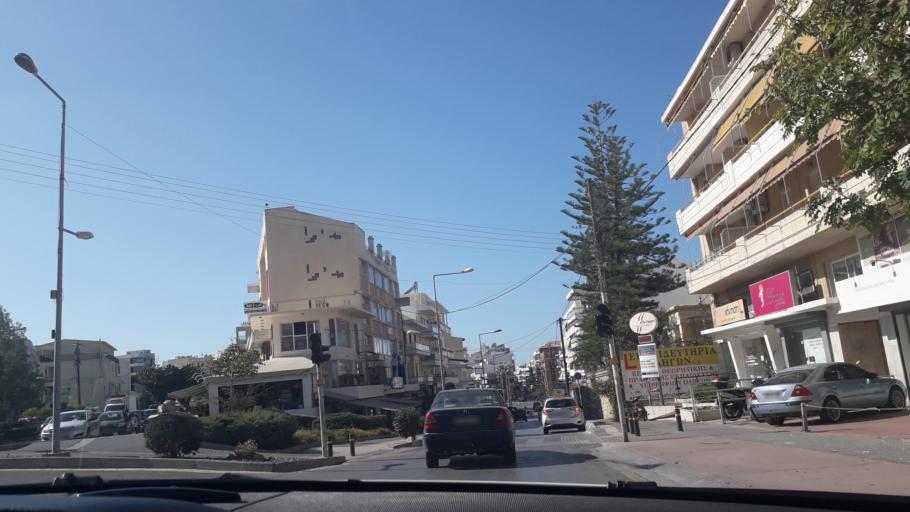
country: GR
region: Crete
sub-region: Nomos Rethymnis
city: Rethymno
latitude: 35.3645
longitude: 24.4848
